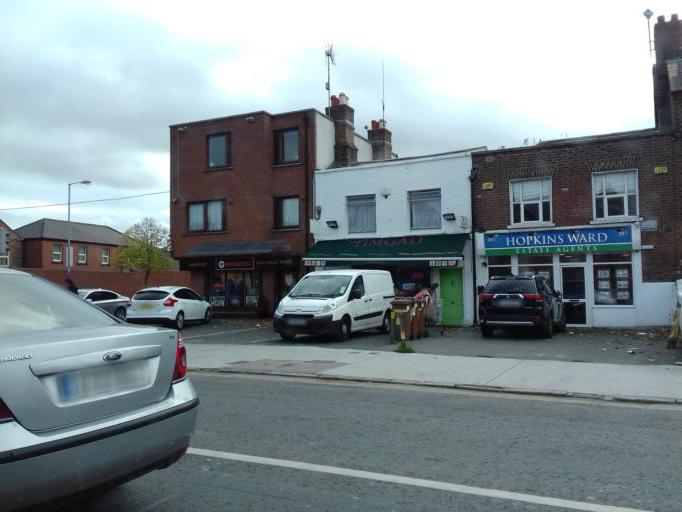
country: IE
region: Leinster
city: Rialto
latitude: 53.3316
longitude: -6.2840
